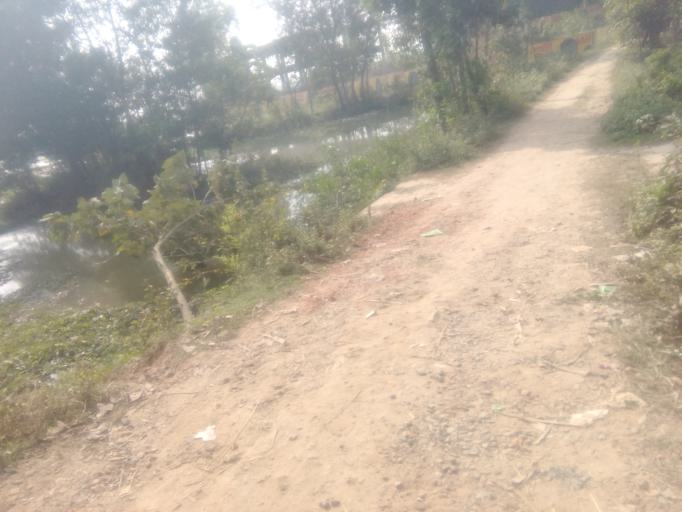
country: IN
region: Tripura
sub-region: West Tripura
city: Sonamura
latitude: 23.3208
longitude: 91.2814
